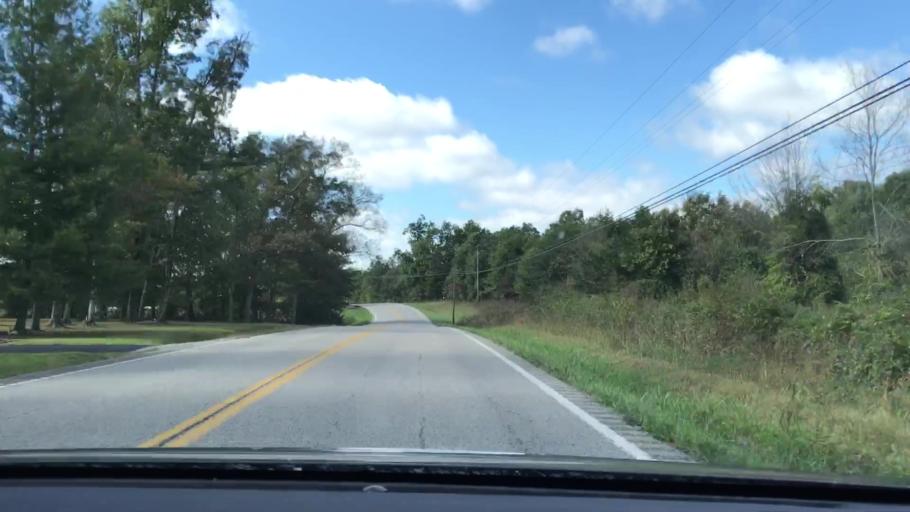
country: US
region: Tennessee
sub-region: Scott County
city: Huntsville
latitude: 36.3457
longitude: -84.6548
